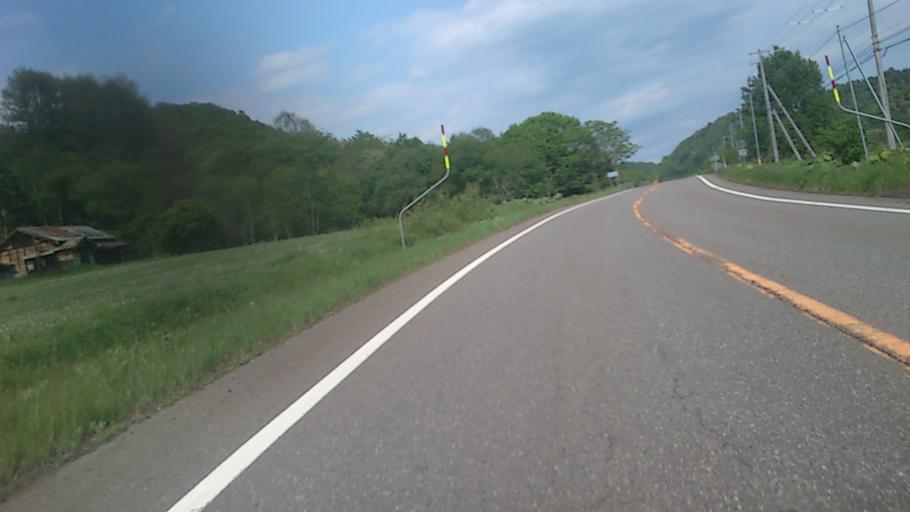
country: JP
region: Hokkaido
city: Kitami
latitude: 43.3427
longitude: 143.7638
